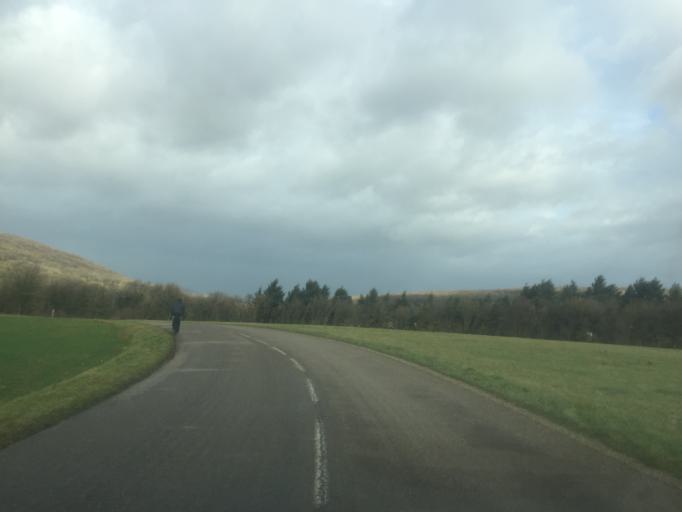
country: FR
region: Franche-Comte
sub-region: Departement du Jura
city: Orchamps
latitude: 47.2151
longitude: 5.6833
